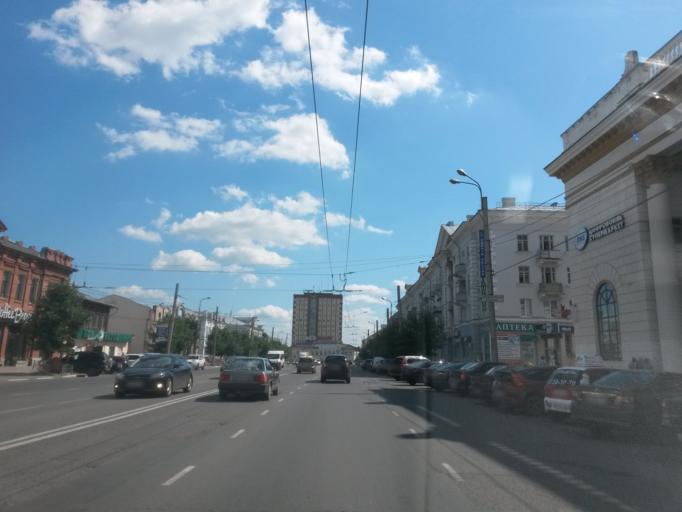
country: RU
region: Ivanovo
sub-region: Gorod Ivanovo
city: Ivanovo
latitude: 56.9972
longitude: 40.9762
